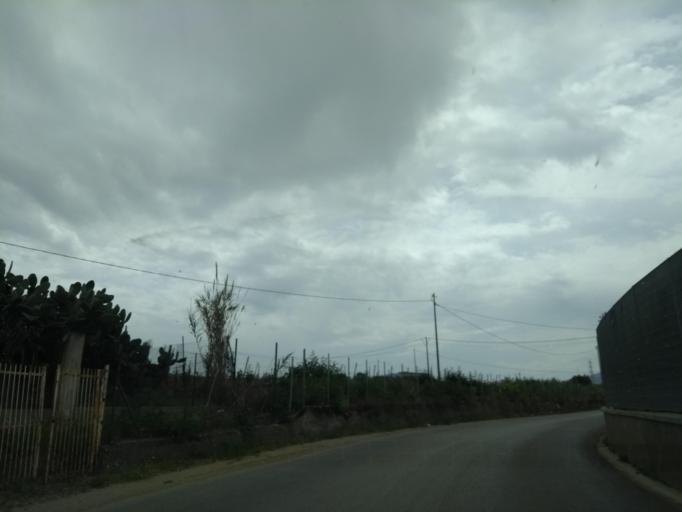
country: IT
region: Sicily
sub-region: Palermo
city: Partinico
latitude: 38.0017
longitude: 13.0680
